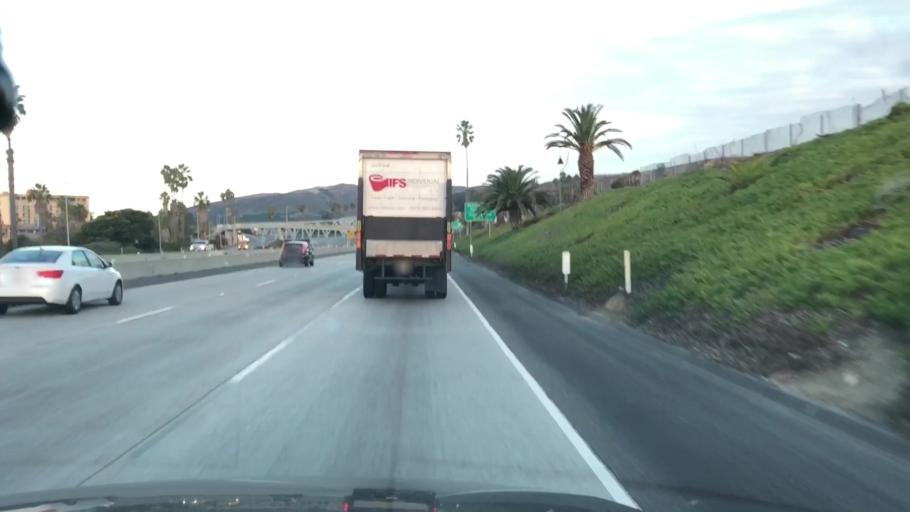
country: US
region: California
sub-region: Ventura County
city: Ventura
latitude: 34.2747
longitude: -119.2863
